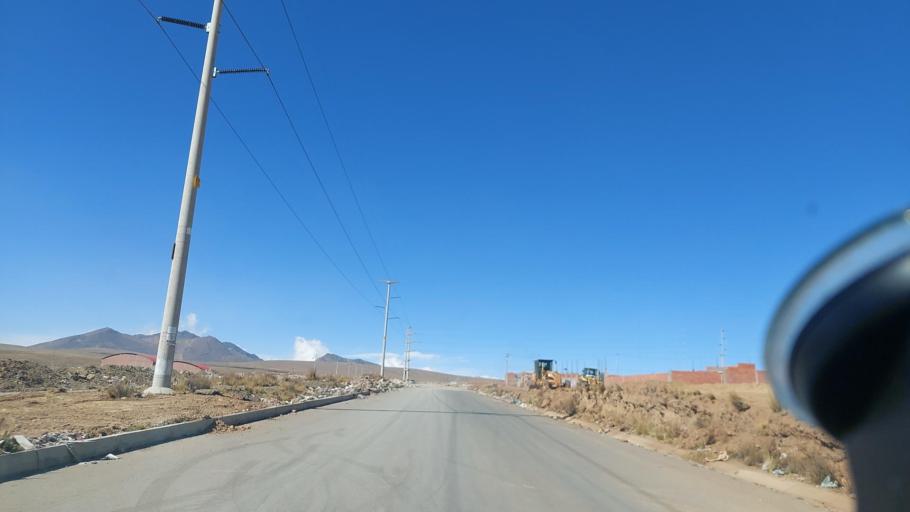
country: BO
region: La Paz
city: La Paz
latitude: -16.4472
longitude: -68.1713
